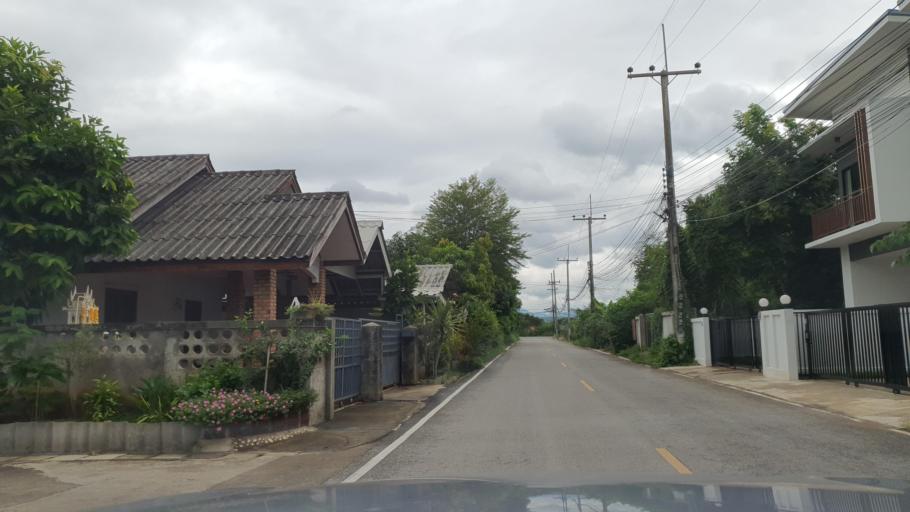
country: TH
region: Chiang Mai
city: Hang Dong
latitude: 18.6807
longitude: 98.9065
